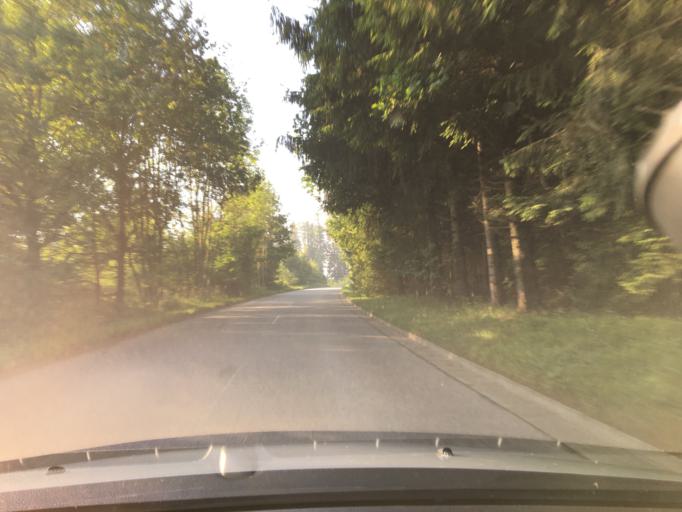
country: DE
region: Bavaria
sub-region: Lower Bavaria
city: Vilsbiburg
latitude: 48.4852
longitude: 12.3176
